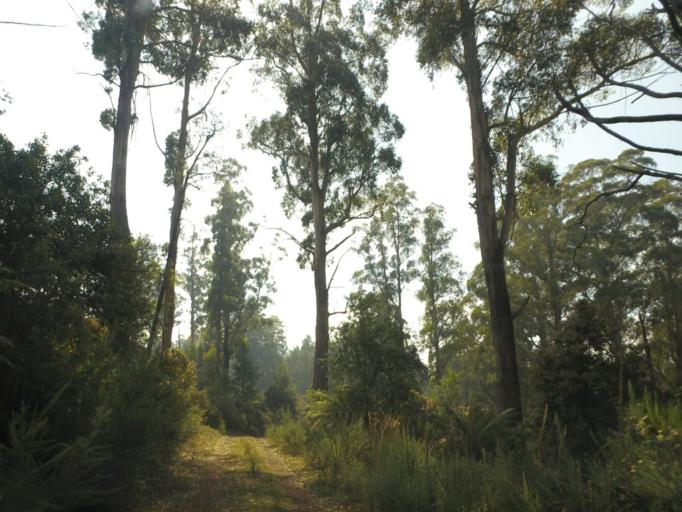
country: AU
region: Victoria
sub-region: Yarra Ranges
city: Healesville
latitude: -37.5625
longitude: 145.6053
